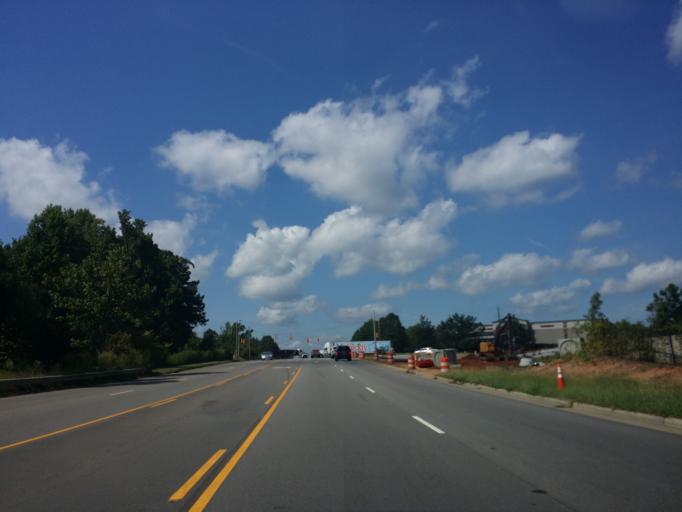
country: US
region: North Carolina
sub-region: Wake County
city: Cary
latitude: 35.9065
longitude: -78.7283
